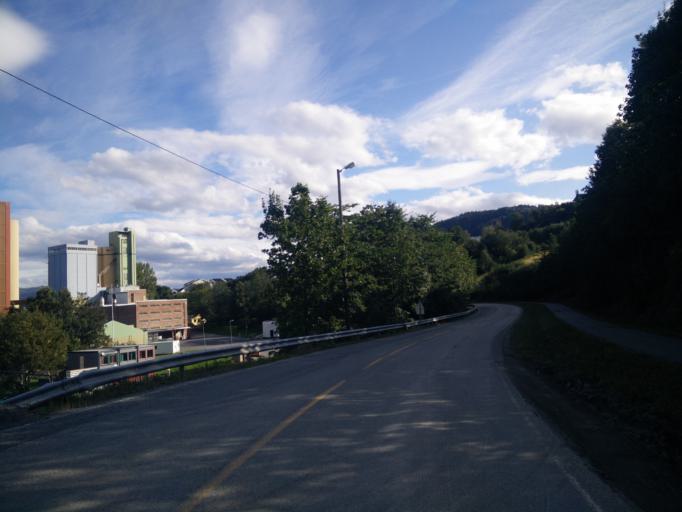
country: NO
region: Sor-Trondelag
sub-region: Skaun
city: Borsa
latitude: 63.3133
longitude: 10.1584
